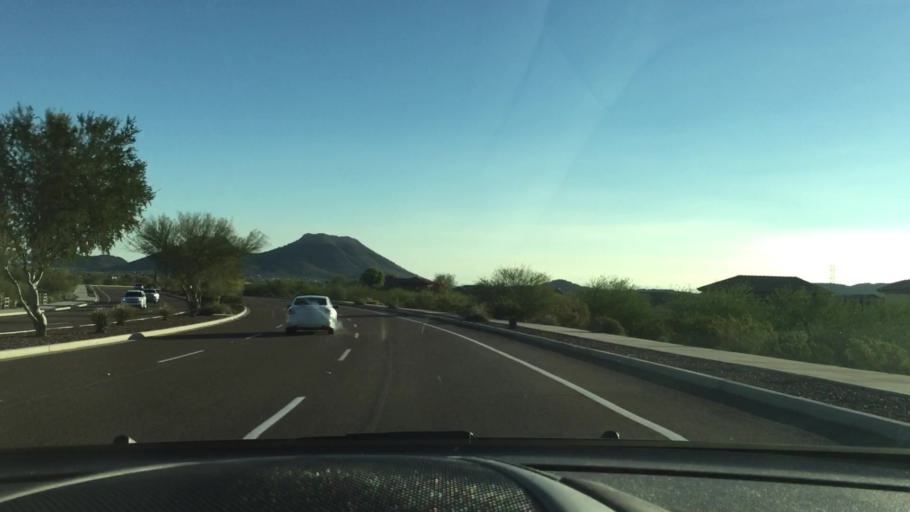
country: US
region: Arizona
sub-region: Maricopa County
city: Sun City
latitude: 33.7070
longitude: -112.2325
